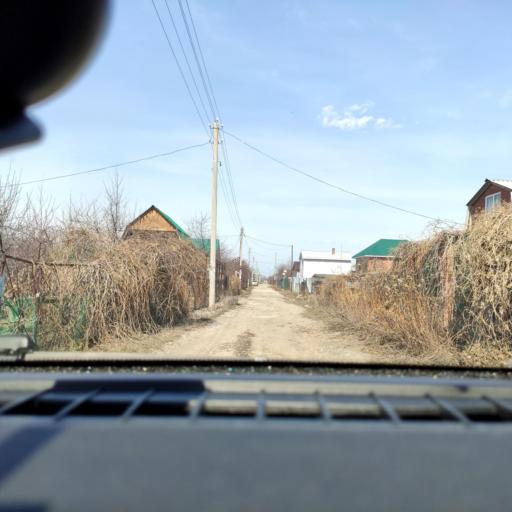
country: RU
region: Samara
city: Podstepki
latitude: 53.5118
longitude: 49.1061
